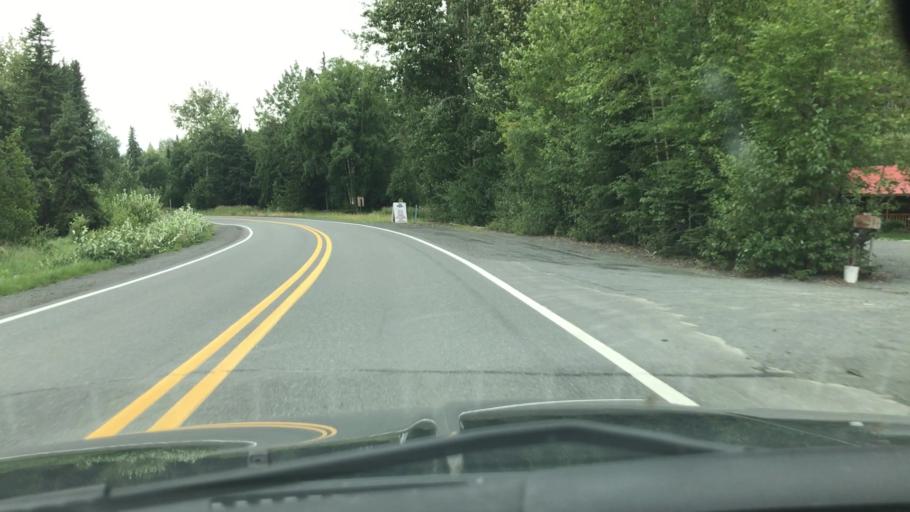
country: US
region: Alaska
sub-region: Kenai Peninsula Borough
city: Seward
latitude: 60.4881
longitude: -149.9777
